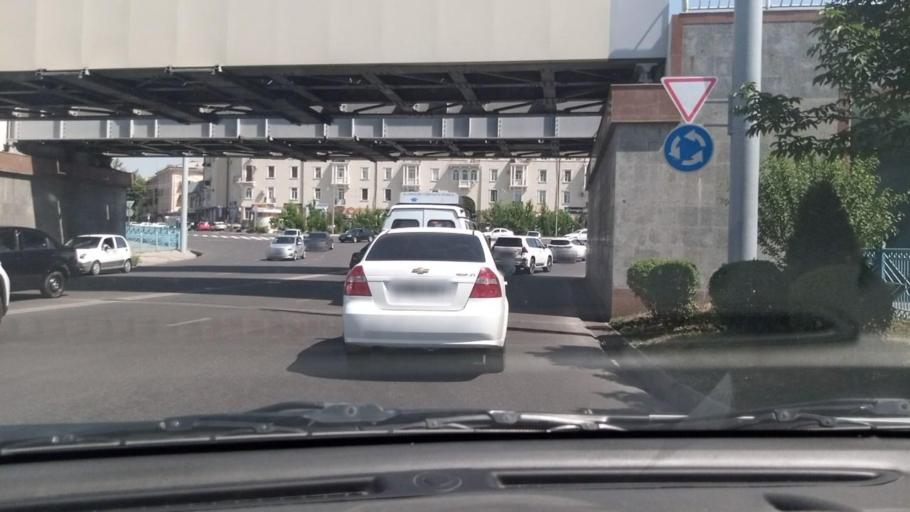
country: UZ
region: Toshkent Shahri
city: Tashkent
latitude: 41.2884
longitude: 69.2824
